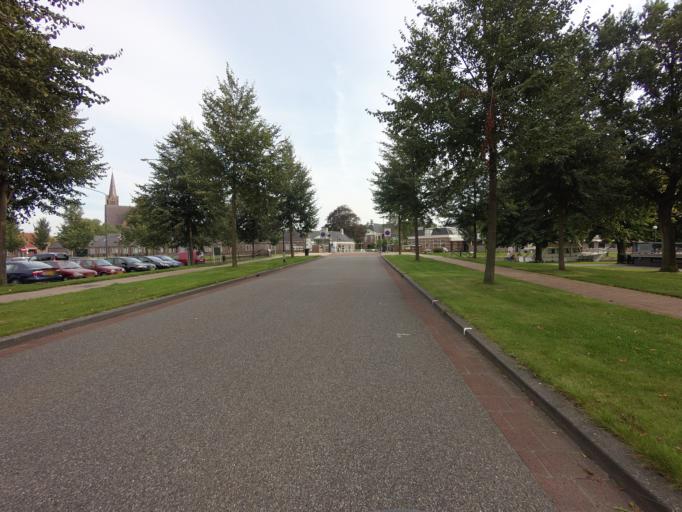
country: NL
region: Friesland
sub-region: Sudwest Fryslan
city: Bolsward
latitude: 53.0639
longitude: 5.5196
